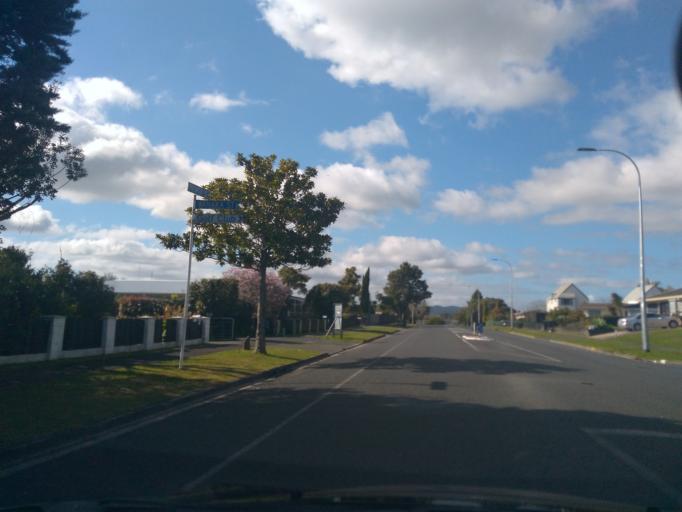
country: NZ
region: Northland
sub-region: Whangarei
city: Whangarei
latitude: -35.6831
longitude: 174.3227
